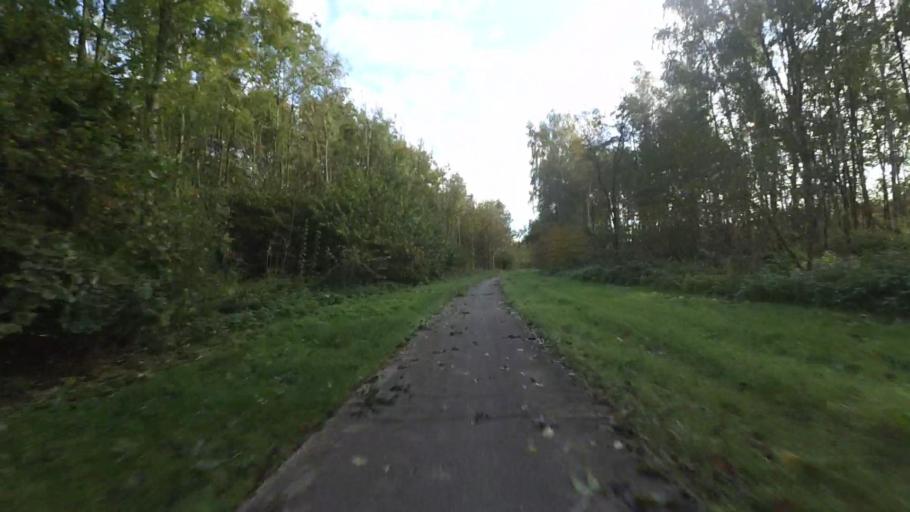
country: NL
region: Utrecht
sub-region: Gemeente Bunschoten
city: Spakenburg
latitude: 52.3135
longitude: 5.3729
